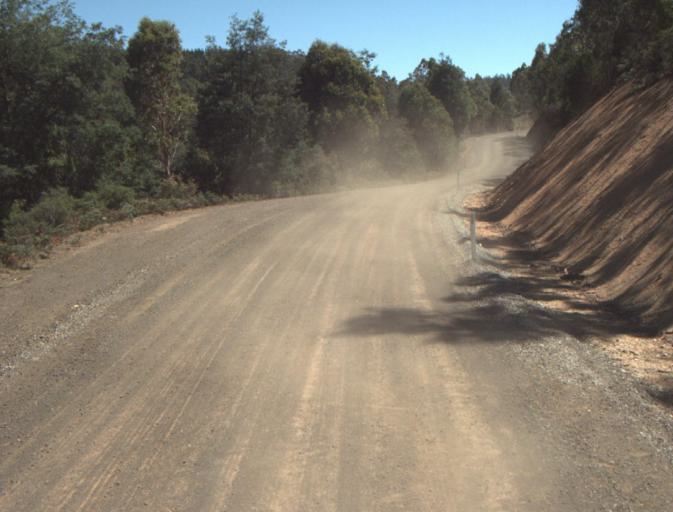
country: AU
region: Tasmania
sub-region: Launceston
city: Newstead
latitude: -41.2945
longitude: 147.3409
